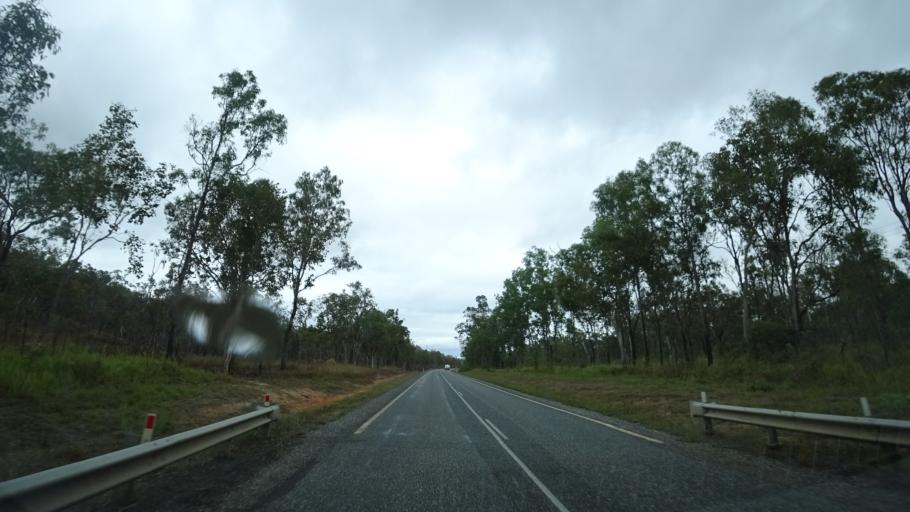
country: AU
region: Queensland
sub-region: Tablelands
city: Mareeba
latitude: -16.7344
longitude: 145.3510
